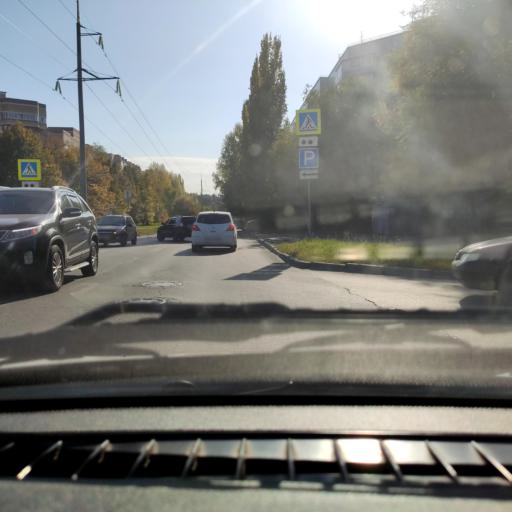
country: RU
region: Samara
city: Tol'yatti
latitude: 53.5110
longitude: 49.4426
